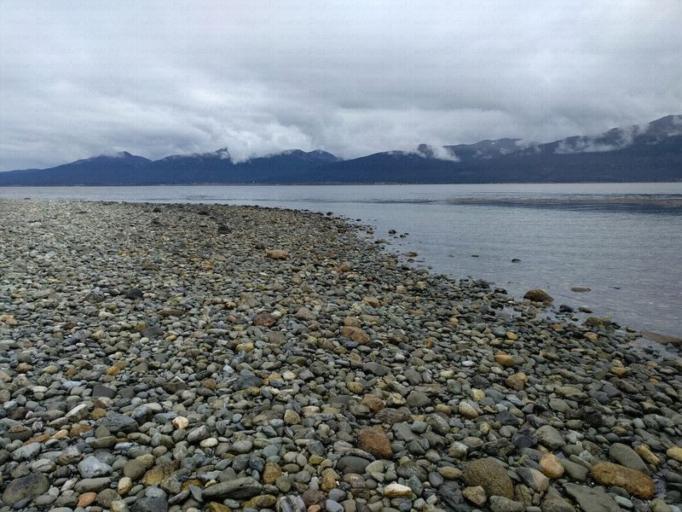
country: AR
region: Tierra del Fuego
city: Ushuaia
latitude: -54.8872
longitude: -67.6911
